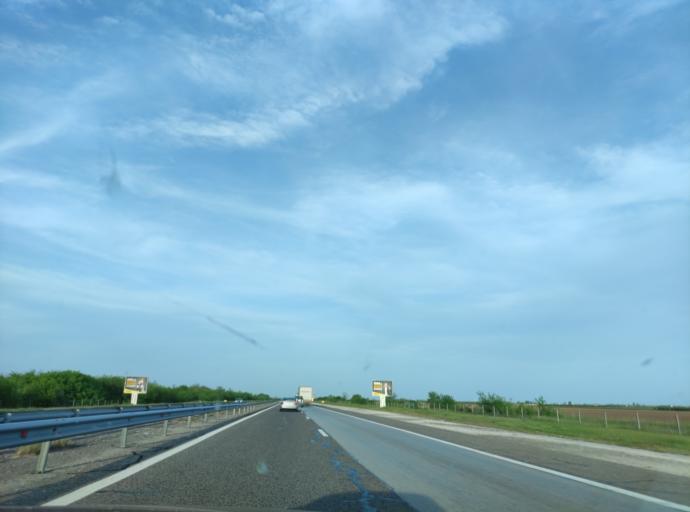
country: BG
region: Plovdiv
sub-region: Obshtina Suedinenie
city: Suedinenie
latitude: 42.2057
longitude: 24.5411
